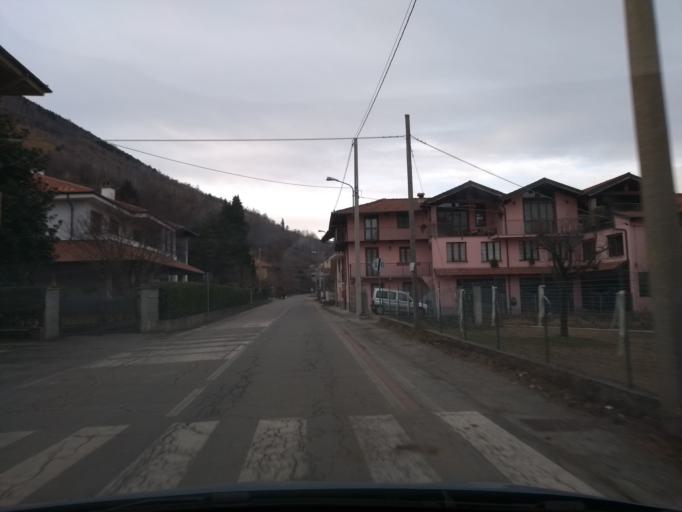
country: IT
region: Piedmont
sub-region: Provincia di Torino
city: Cafasse
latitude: 45.2558
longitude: 7.5073
